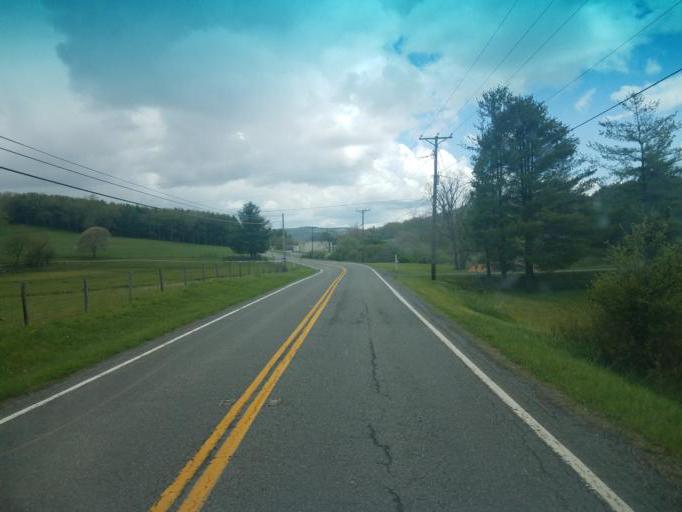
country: US
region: Virginia
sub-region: Bland County
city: Bland
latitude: 37.0878
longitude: -81.1420
